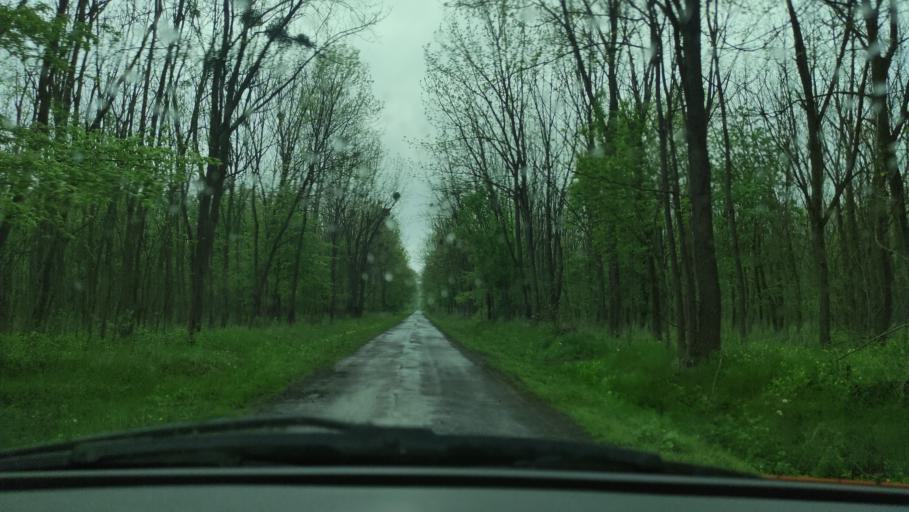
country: HU
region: Baranya
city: Mohacs
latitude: 45.9116
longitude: 18.7481
